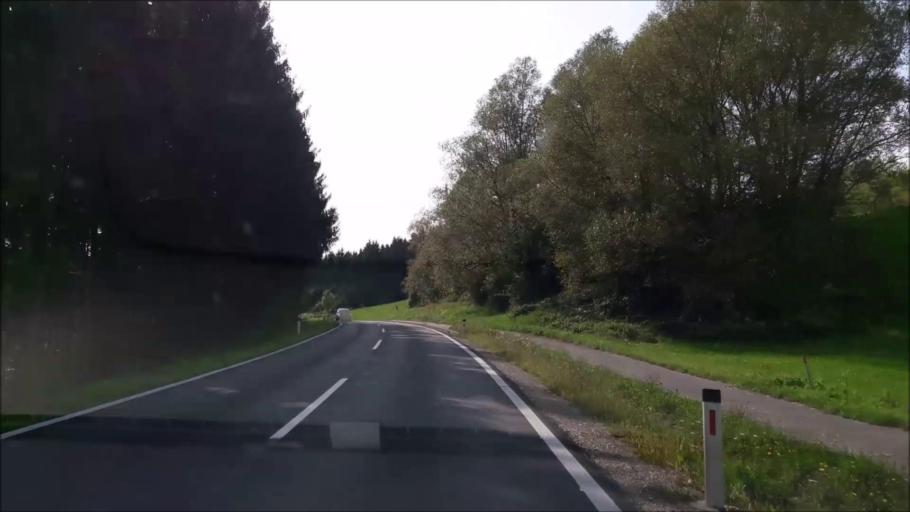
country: AT
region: Styria
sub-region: Politischer Bezirk Weiz
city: Floing
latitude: 47.2430
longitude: 15.7442
